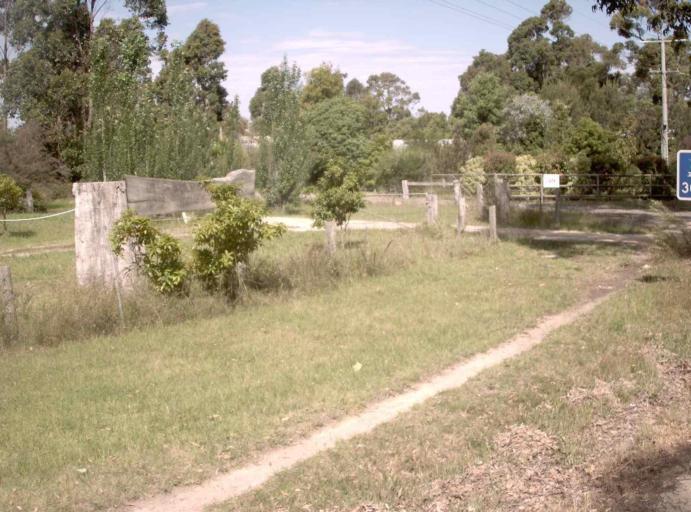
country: AU
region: New South Wales
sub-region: Bega Valley
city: Eden
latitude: -37.5517
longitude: 149.7388
